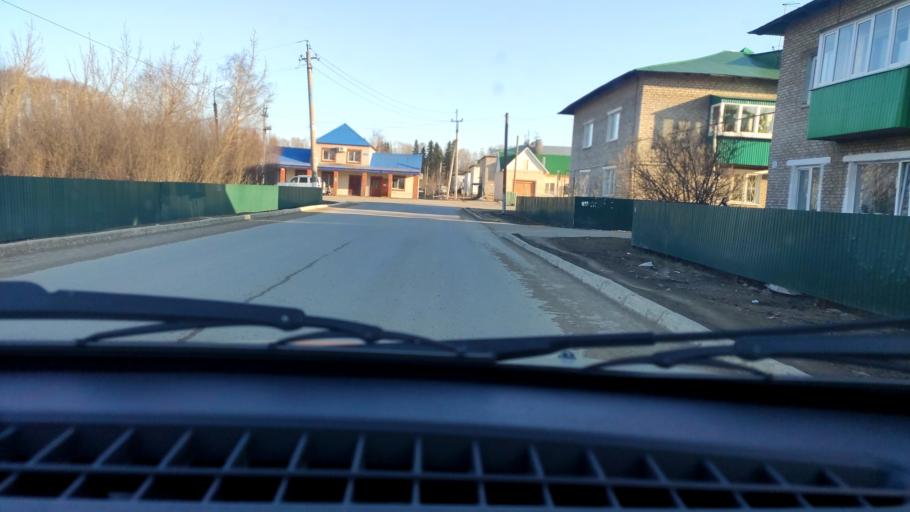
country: RU
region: Bashkortostan
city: Iglino
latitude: 54.8330
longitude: 56.4171
